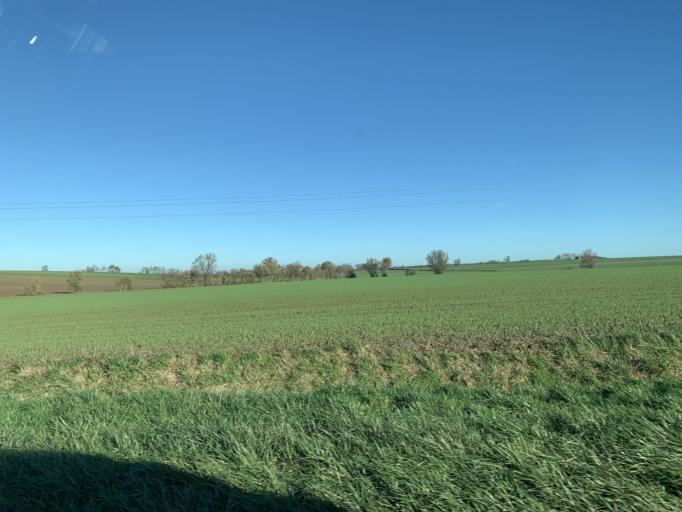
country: FR
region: Nord-Pas-de-Calais
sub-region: Departement du Nord
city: Escaudoeuvres
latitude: 50.1580
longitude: 3.3079
